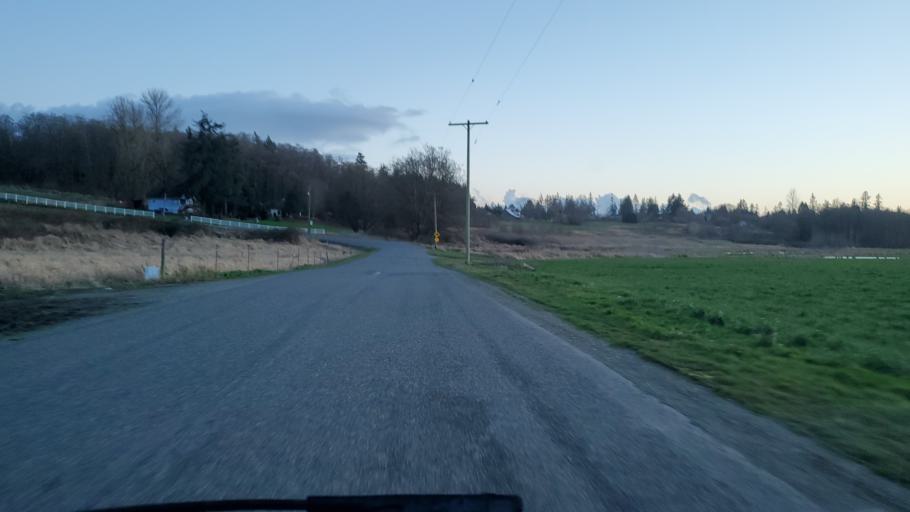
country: US
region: Washington
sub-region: Skagit County
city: Burlington
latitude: 48.4616
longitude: -122.2975
